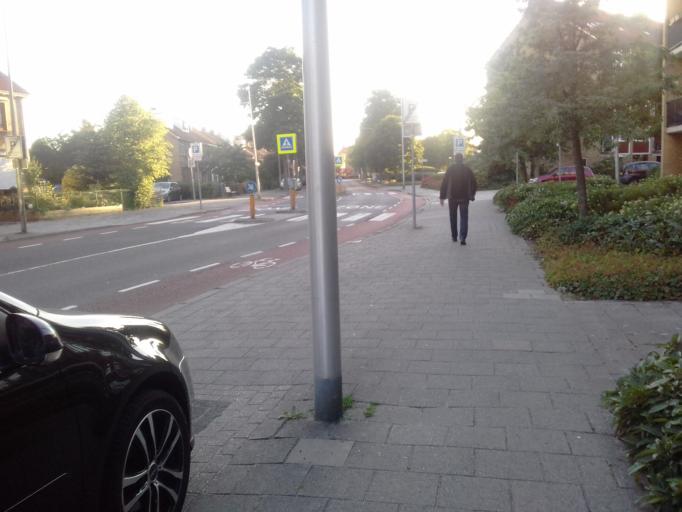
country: NL
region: North Holland
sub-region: Gemeente Diemen
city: Diemen
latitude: 52.3417
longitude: 4.9599
